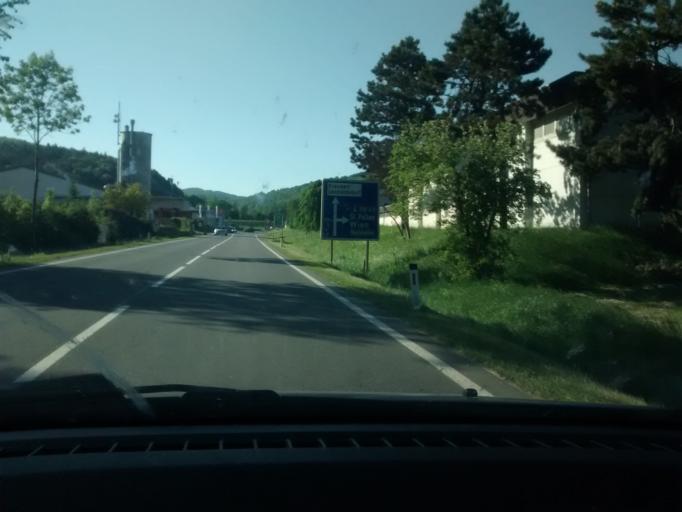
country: AT
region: Lower Austria
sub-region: Politischer Bezirk Baden
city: Alland
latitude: 48.0658
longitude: 16.0656
